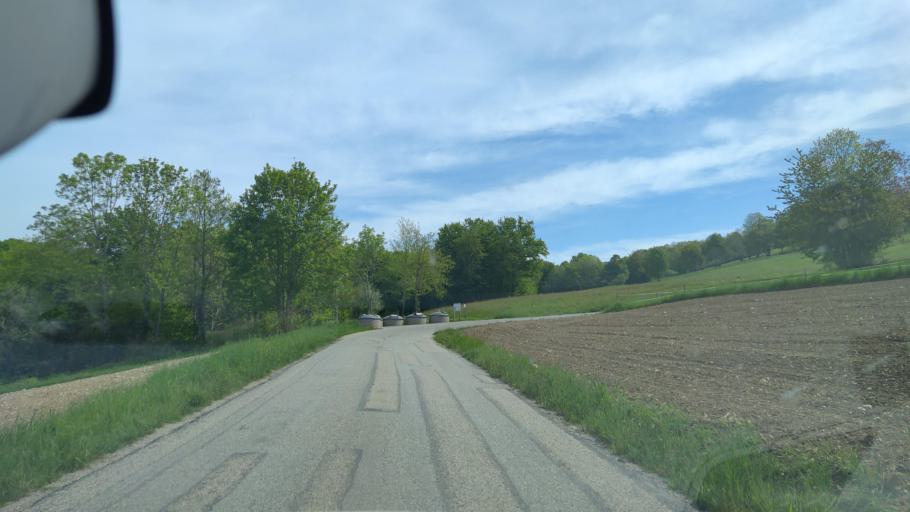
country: FR
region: Rhone-Alpes
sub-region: Departement de la Savoie
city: Mouxy
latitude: 45.7002
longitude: 5.9527
